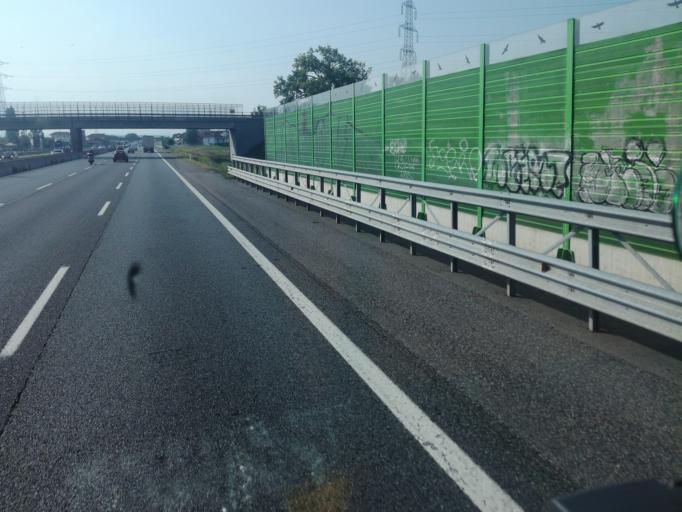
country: IT
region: Piedmont
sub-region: Provincia di Torino
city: Nichelino
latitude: 44.9813
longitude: 7.6464
